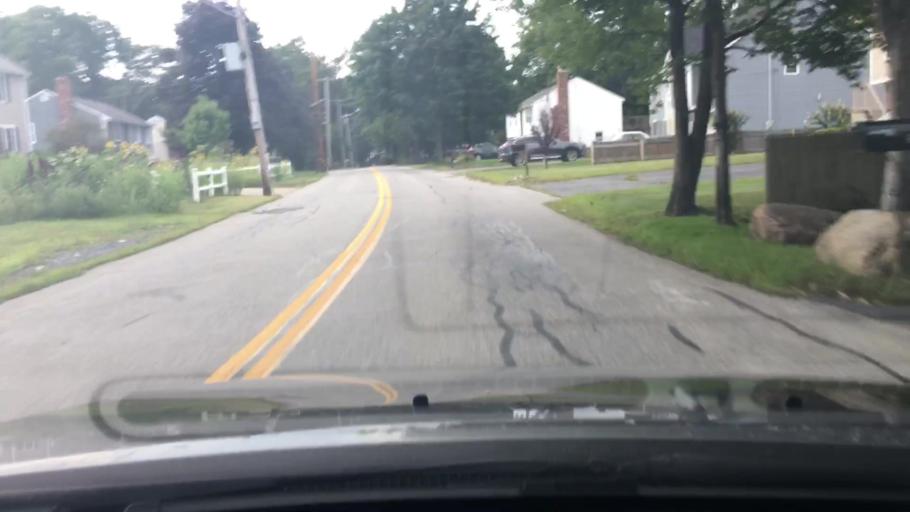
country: US
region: Massachusetts
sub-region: Worcester County
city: Hopedale
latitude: 42.1605
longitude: -71.5381
